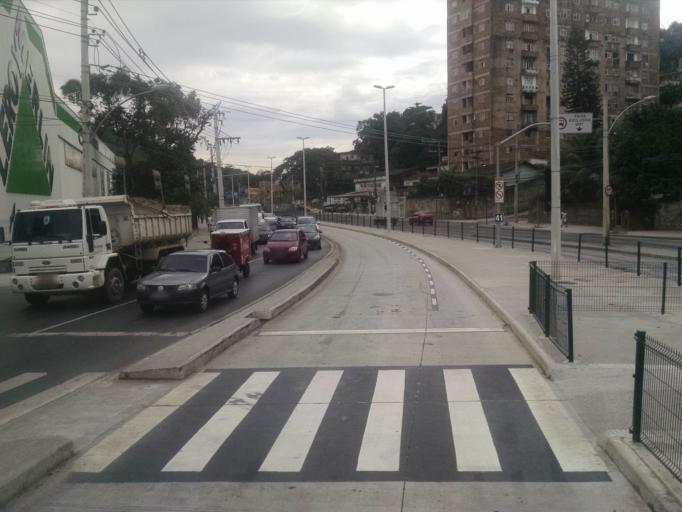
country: BR
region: Rio de Janeiro
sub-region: Sao Joao De Meriti
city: Sao Joao de Meriti
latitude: -22.9147
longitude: -43.3609
